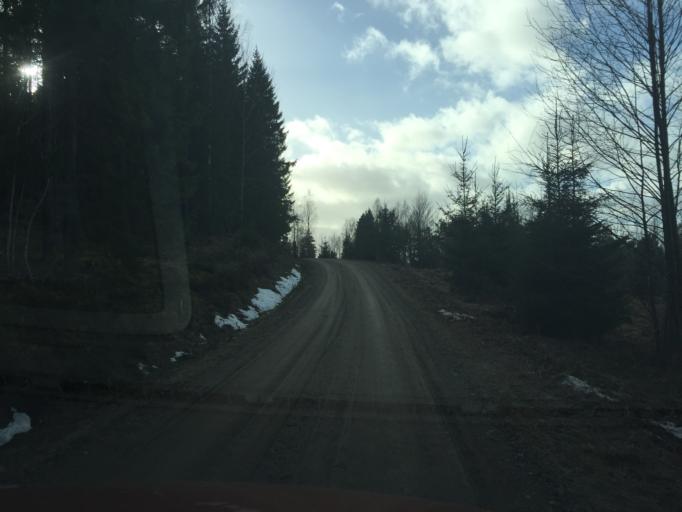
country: SE
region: Soedermanland
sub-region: Vingakers Kommun
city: Vingaker
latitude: 58.9851
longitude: 15.7231
